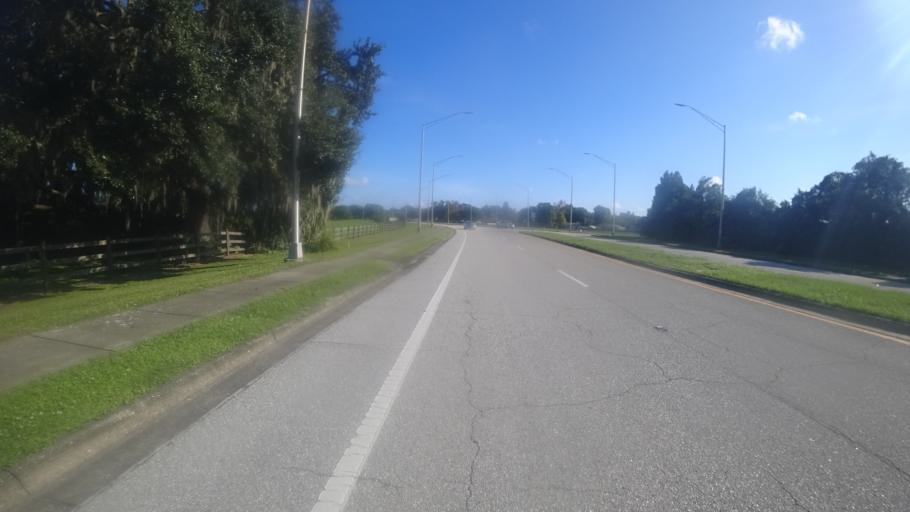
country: US
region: Florida
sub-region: Manatee County
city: Ellenton
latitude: 27.4974
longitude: -82.4830
